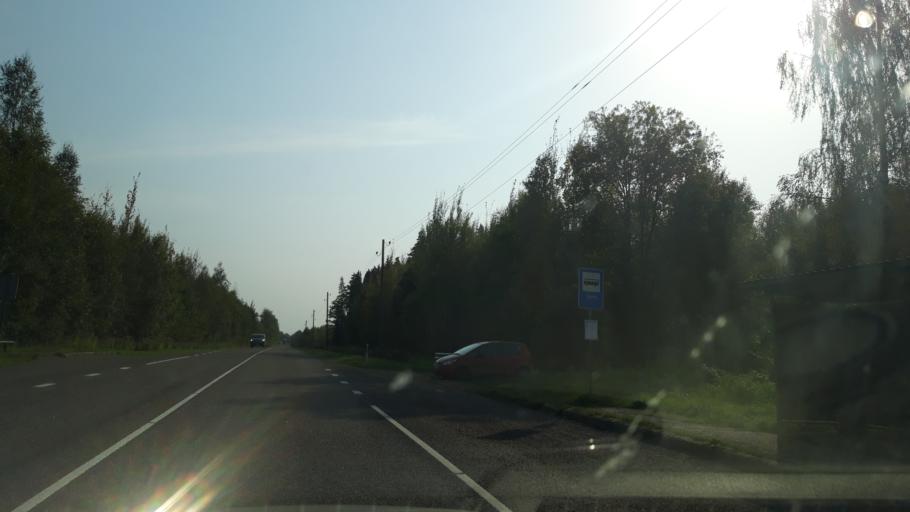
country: LV
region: Burtnieki
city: Matisi
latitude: 57.6379
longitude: 25.2532
